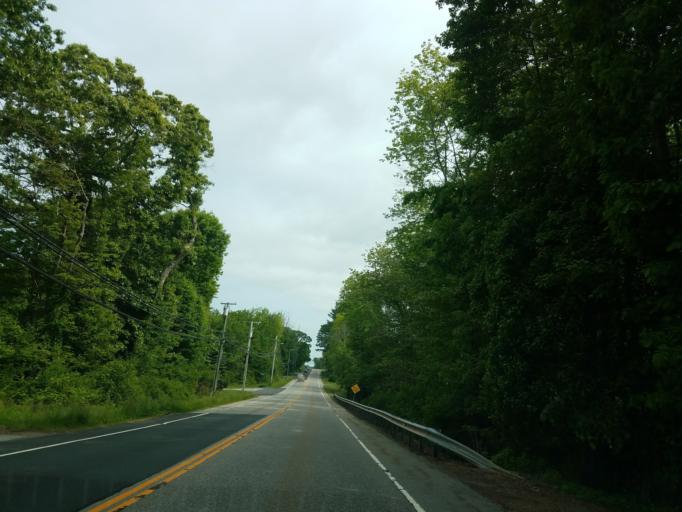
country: US
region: Connecticut
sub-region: Hartford County
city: Manchester
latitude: 41.7329
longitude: -72.4350
